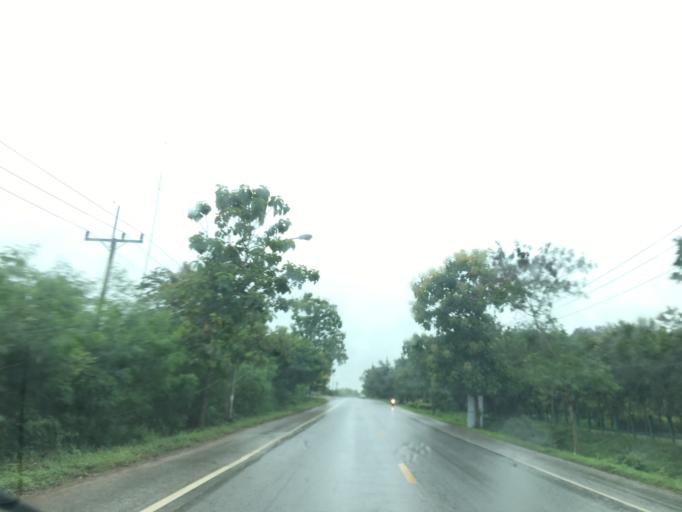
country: TH
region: Chiang Rai
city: Wiang Chai
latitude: 19.7865
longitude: 99.9096
